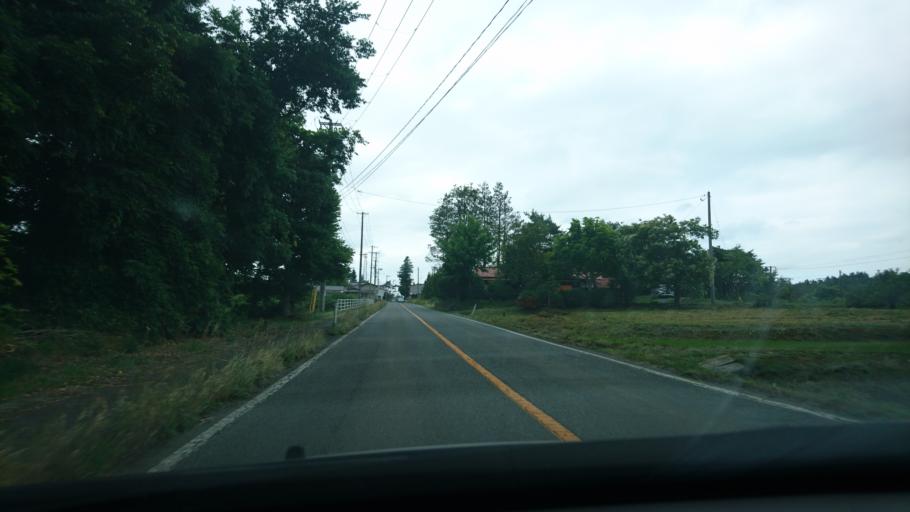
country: JP
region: Iwate
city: Ichinoseki
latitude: 38.8178
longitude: 141.1816
